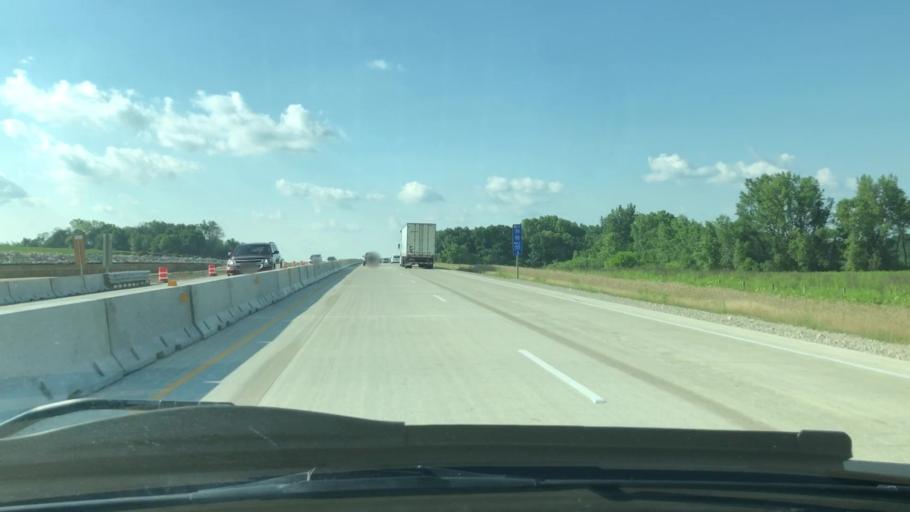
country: US
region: Wisconsin
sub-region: Jefferson County
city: Cambridge
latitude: 42.9346
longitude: -89.0880
